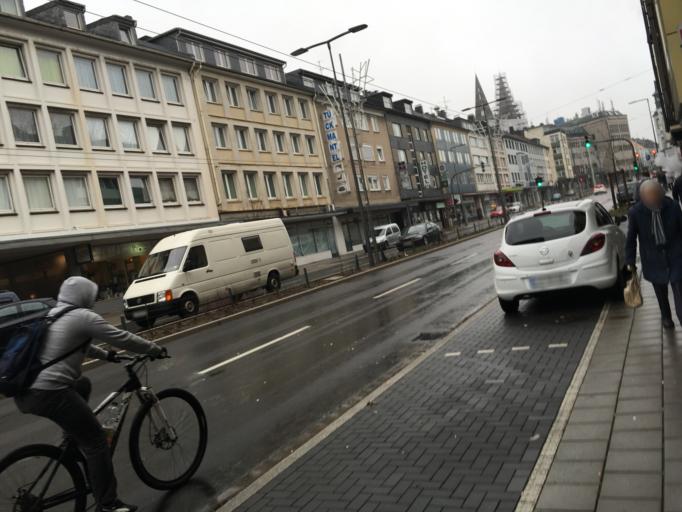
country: DE
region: North Rhine-Westphalia
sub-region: Regierungsbezirk Dusseldorf
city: Solingen
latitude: 51.1764
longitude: 7.0840
